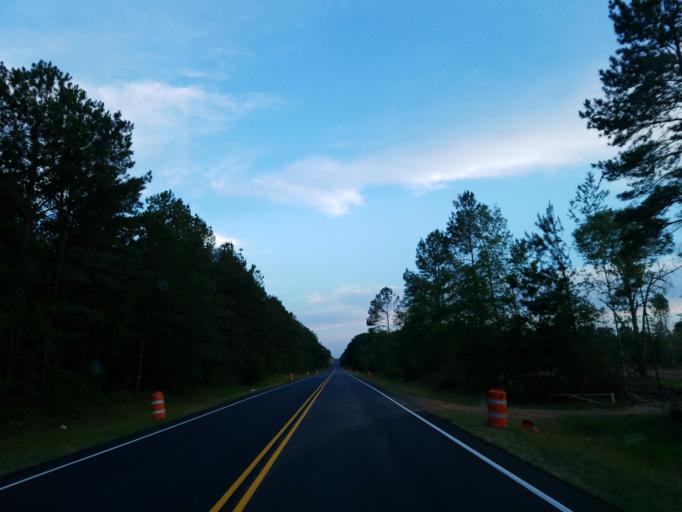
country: US
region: Georgia
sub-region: Turner County
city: Ashburn
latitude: 31.7263
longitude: -83.8081
